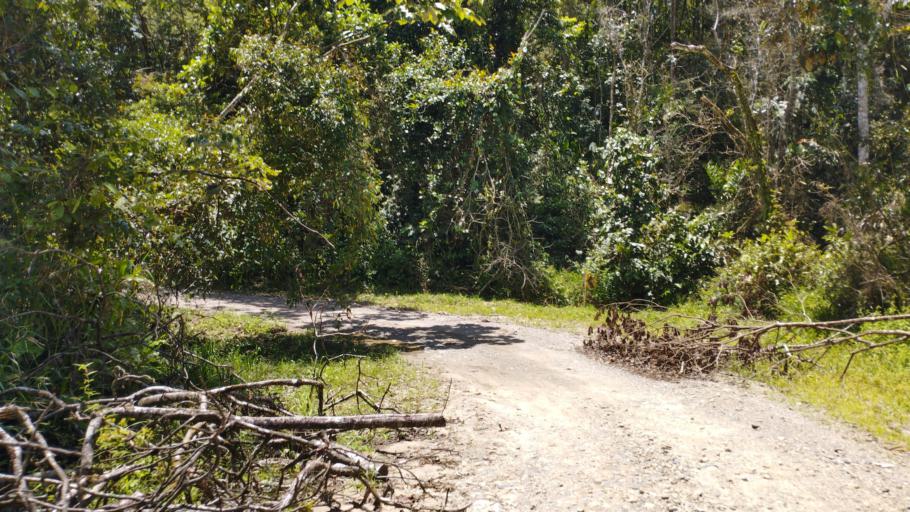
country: CO
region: Boyaca
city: San Luis de Gaceno
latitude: 4.7739
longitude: -73.1360
